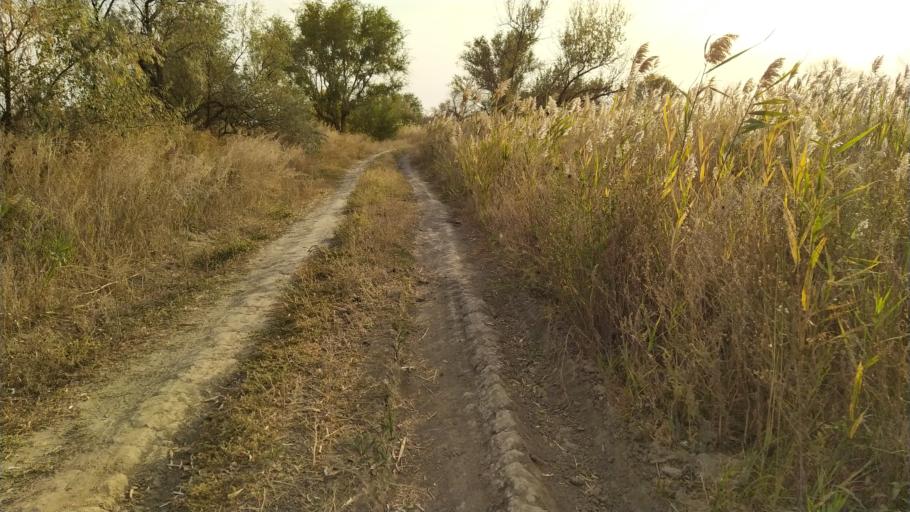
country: RU
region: Rostov
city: Kuleshovka
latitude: 47.1224
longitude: 39.6031
